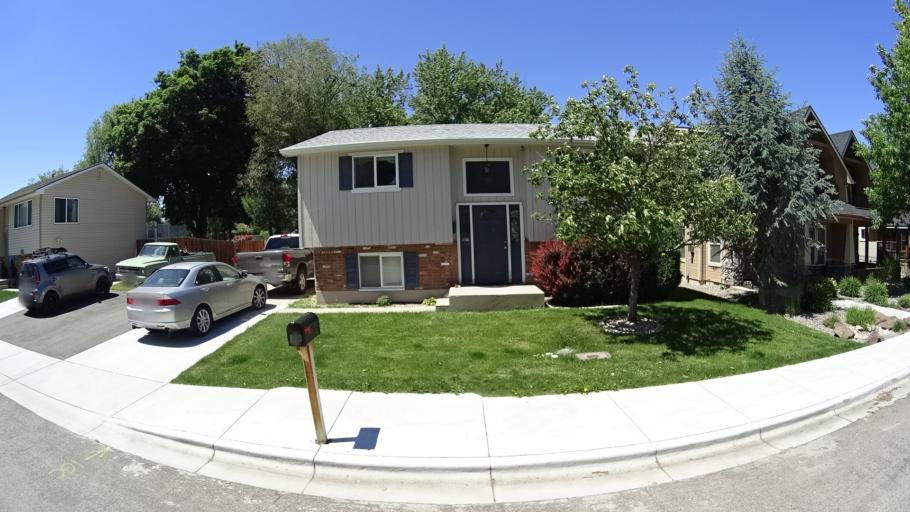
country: US
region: Idaho
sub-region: Ada County
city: Boise
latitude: 43.5821
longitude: -116.2187
